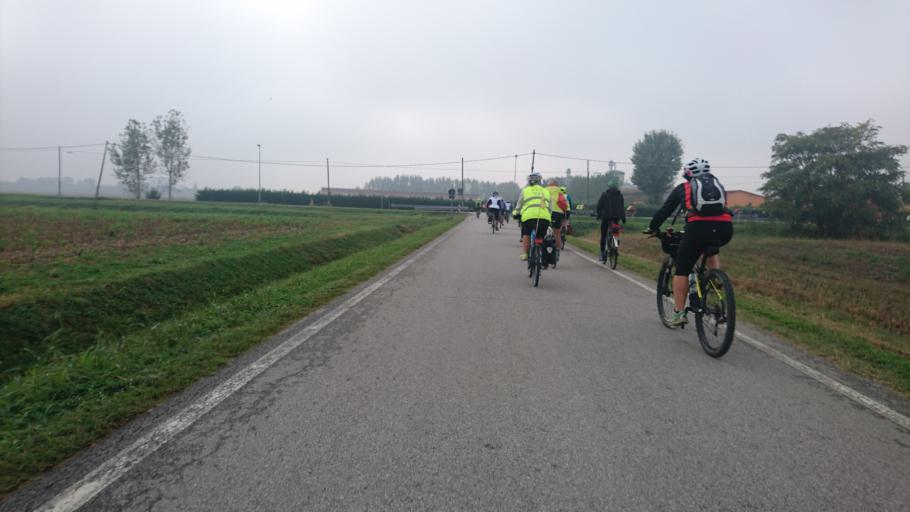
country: IT
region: Veneto
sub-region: Provincia di Padova
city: Stanghella
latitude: 45.1570
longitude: 11.7882
